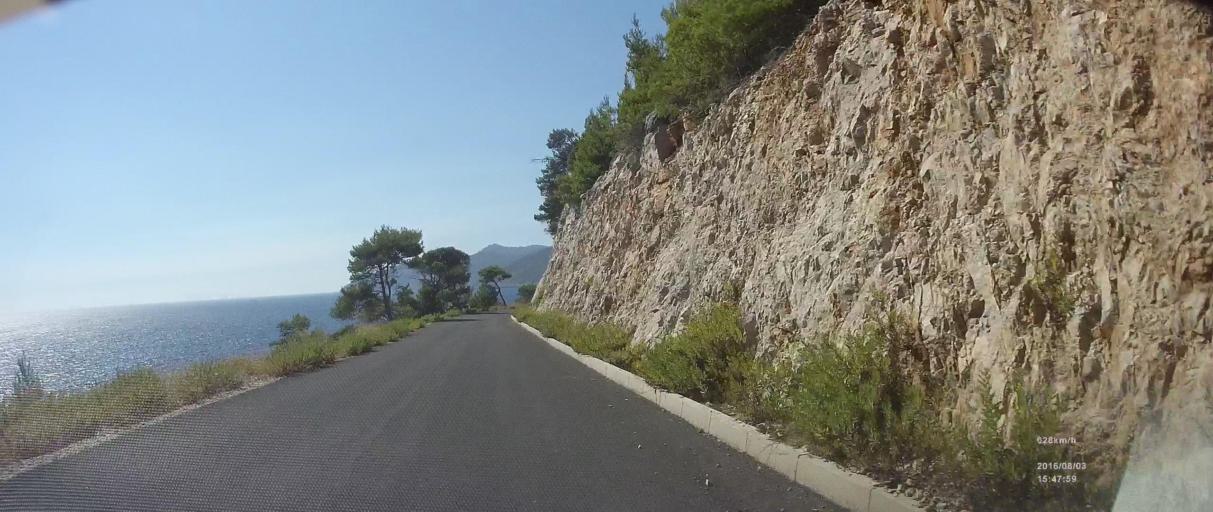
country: HR
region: Dubrovacko-Neretvanska
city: Blato
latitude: 42.7354
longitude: 17.5055
